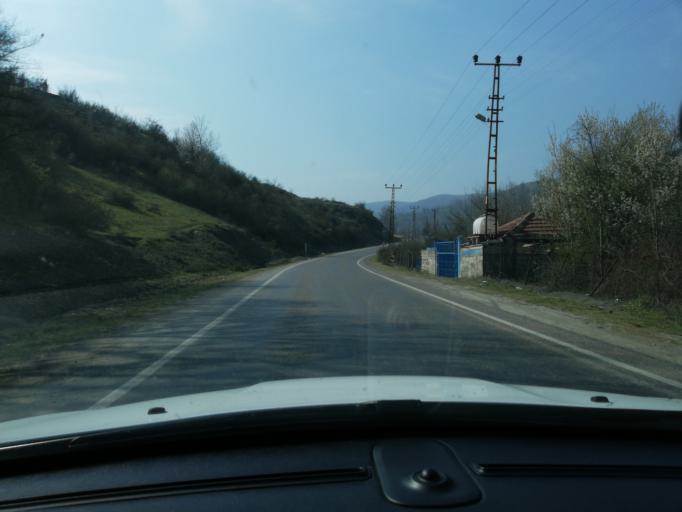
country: TR
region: Karabuk
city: Yenice
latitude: 41.2489
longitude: 32.3577
